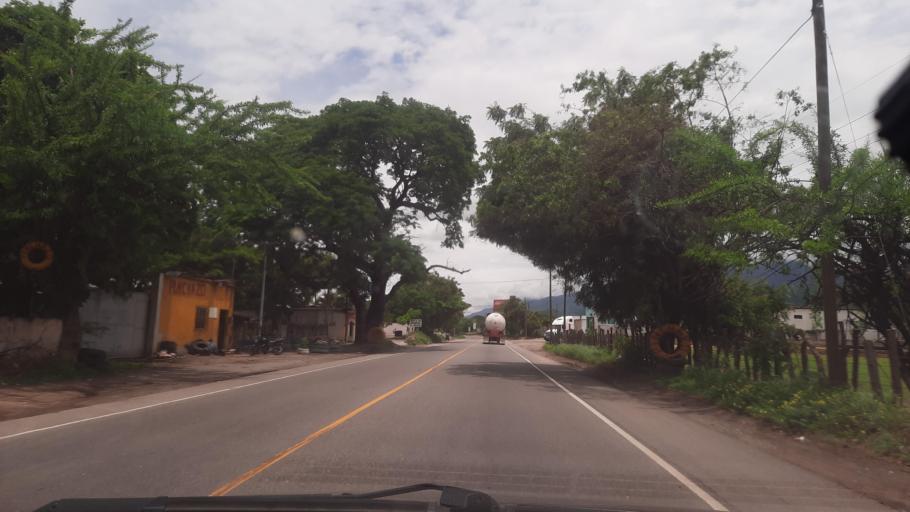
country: GT
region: Zacapa
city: Rio Hondo
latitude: 15.0852
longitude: -89.4753
